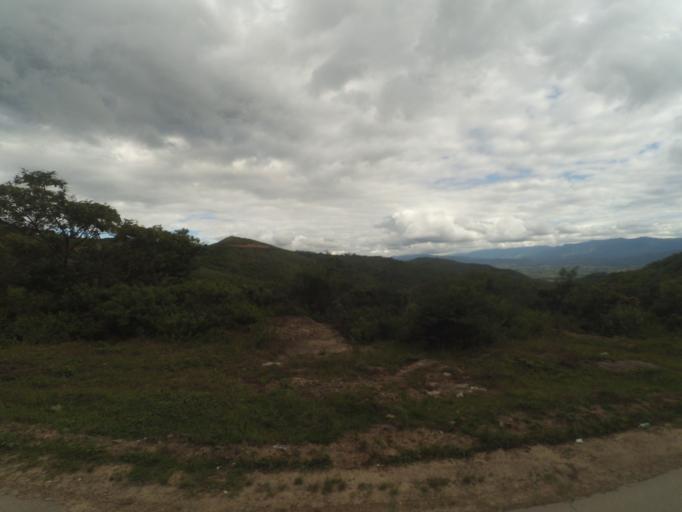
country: BO
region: Santa Cruz
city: Samaipata
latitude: -18.1754
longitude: -63.8721
